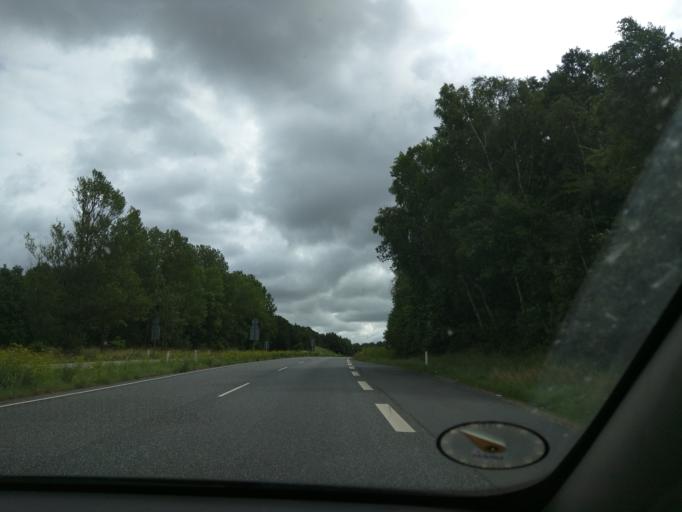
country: DK
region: Zealand
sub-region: Holbaek Kommune
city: Jyderup
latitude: 55.6699
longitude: 11.3542
